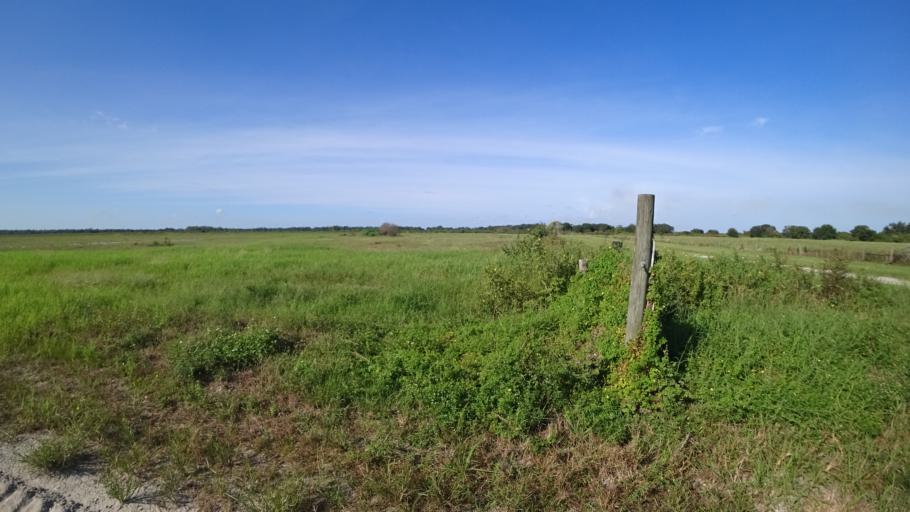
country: US
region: Florida
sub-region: Sarasota County
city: The Meadows
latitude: 27.4449
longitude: -82.3403
